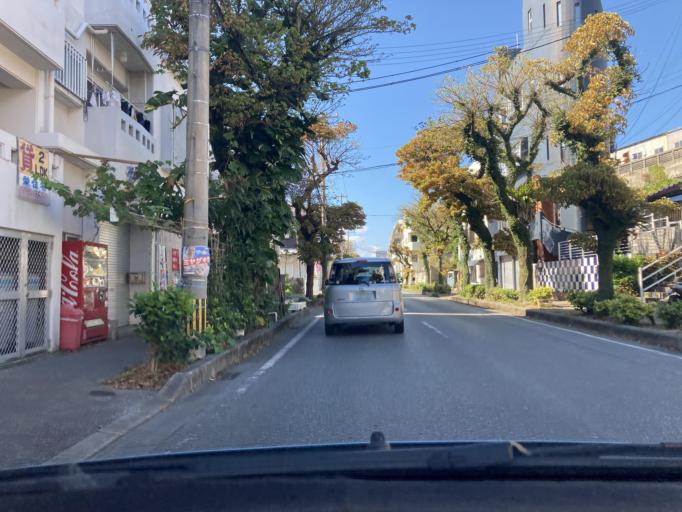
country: JP
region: Okinawa
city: Naha-shi
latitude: 26.2399
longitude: 127.6965
